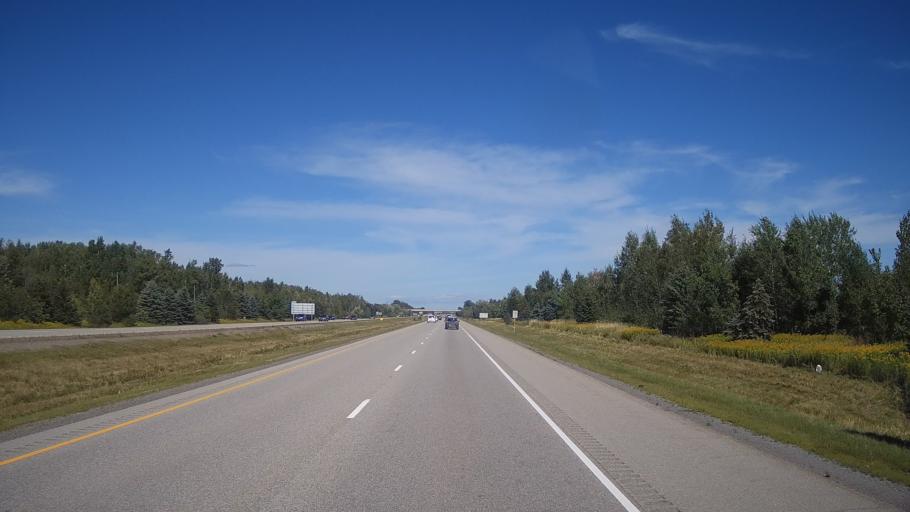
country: CA
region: Ontario
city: Bells Corners
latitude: 45.2197
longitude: -75.7445
